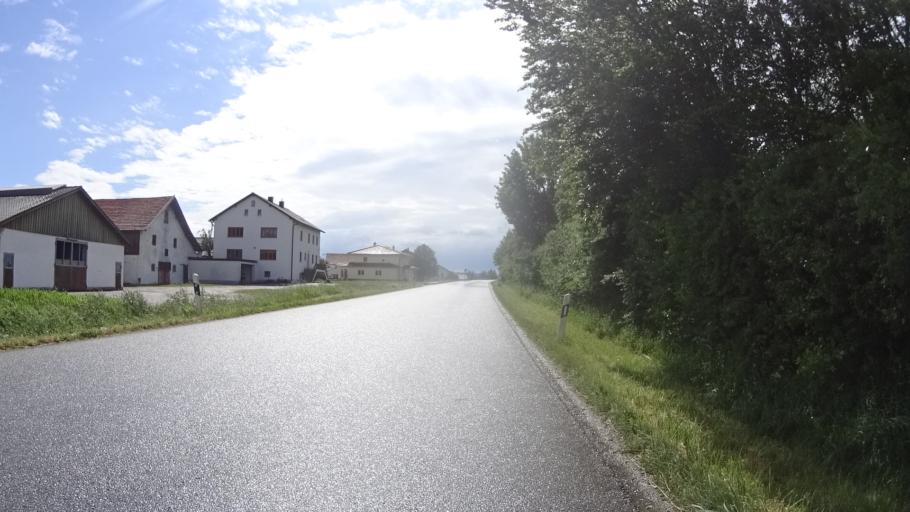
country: DE
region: Bavaria
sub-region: Upper Bavaria
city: Egglkofen
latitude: 48.4460
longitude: 12.4560
